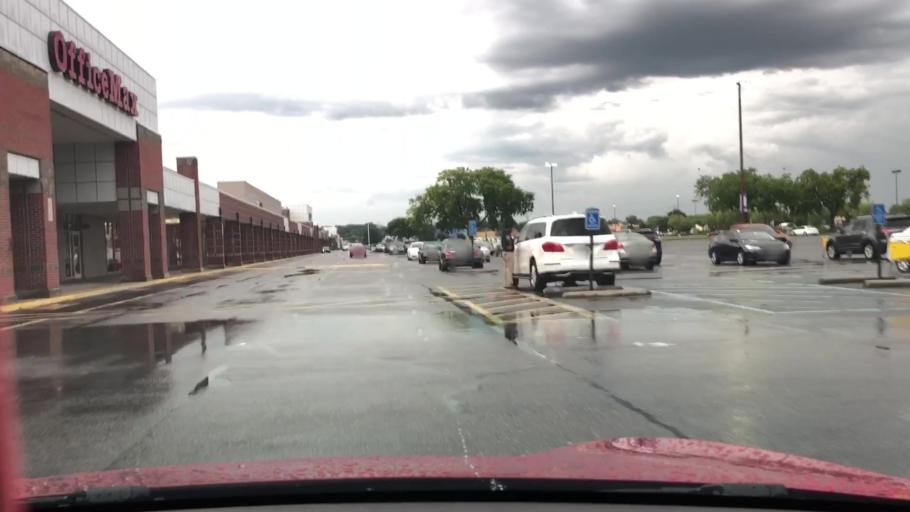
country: US
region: Virginia
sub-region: City of Chesapeake
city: Chesapeake
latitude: 36.8596
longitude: -76.2054
